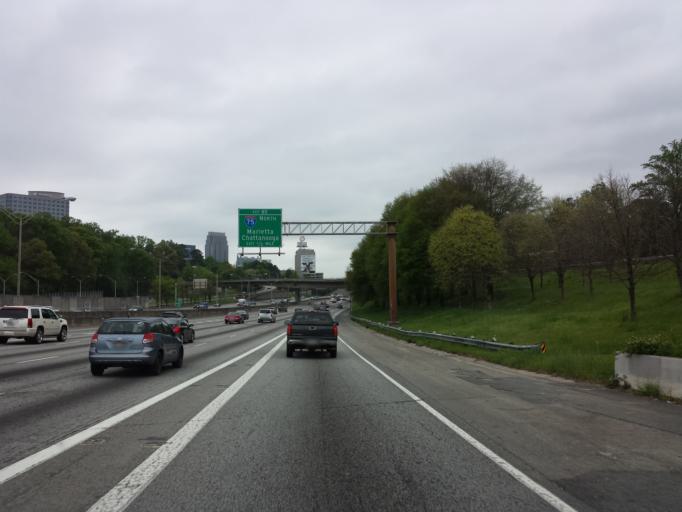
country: US
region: Georgia
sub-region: DeKalb County
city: Druid Hills
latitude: 33.8037
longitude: -84.3850
